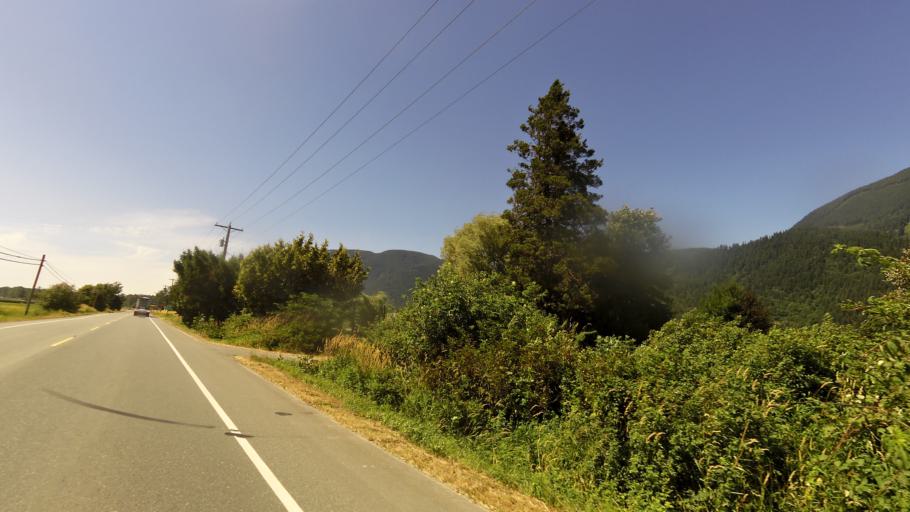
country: CA
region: British Columbia
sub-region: Fraser Valley Regional District
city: Chilliwack
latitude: 49.1693
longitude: -122.1217
